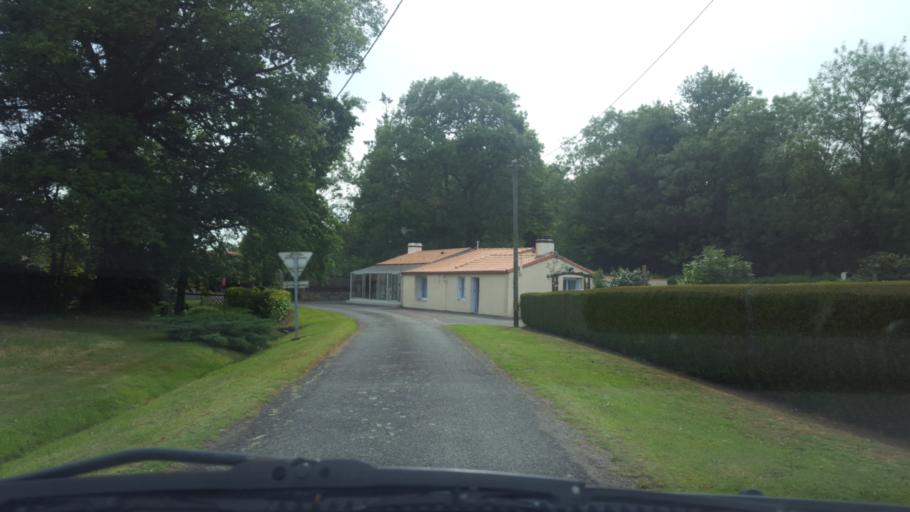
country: FR
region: Pays de la Loire
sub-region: Departement de la Loire-Atlantique
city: La Limouziniere
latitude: 46.9896
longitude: -1.5869
